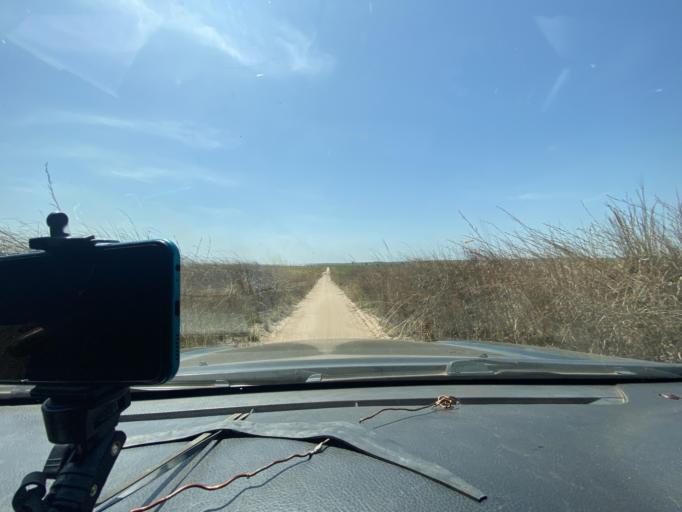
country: CD
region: Kasai-Oriental
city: Kabinda
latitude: -5.9370
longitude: 24.8169
